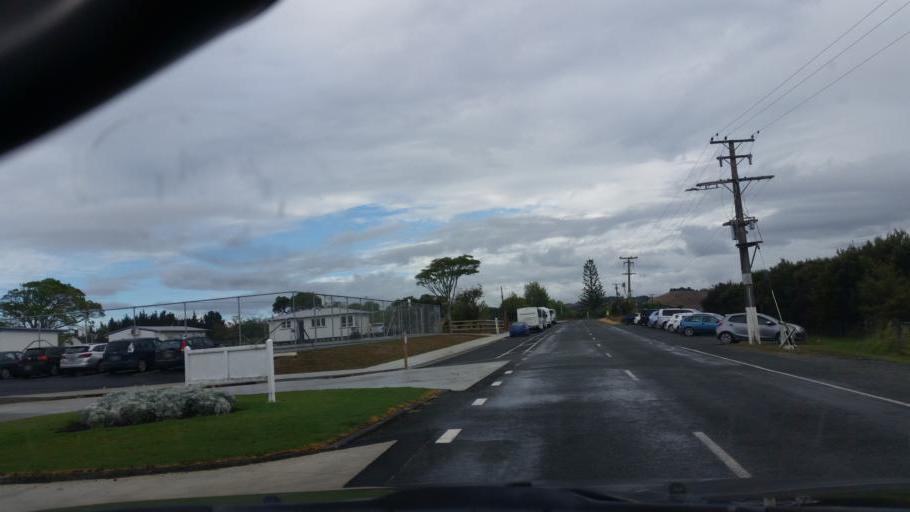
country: NZ
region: Auckland
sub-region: Auckland
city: Wellsford
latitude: -36.1168
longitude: 174.3655
